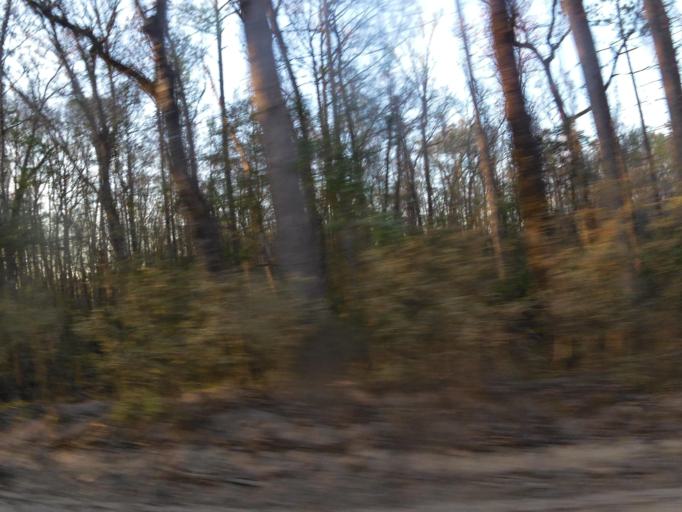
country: US
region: Florida
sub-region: Clay County
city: Green Cove Springs
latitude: 29.8367
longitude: -81.7992
